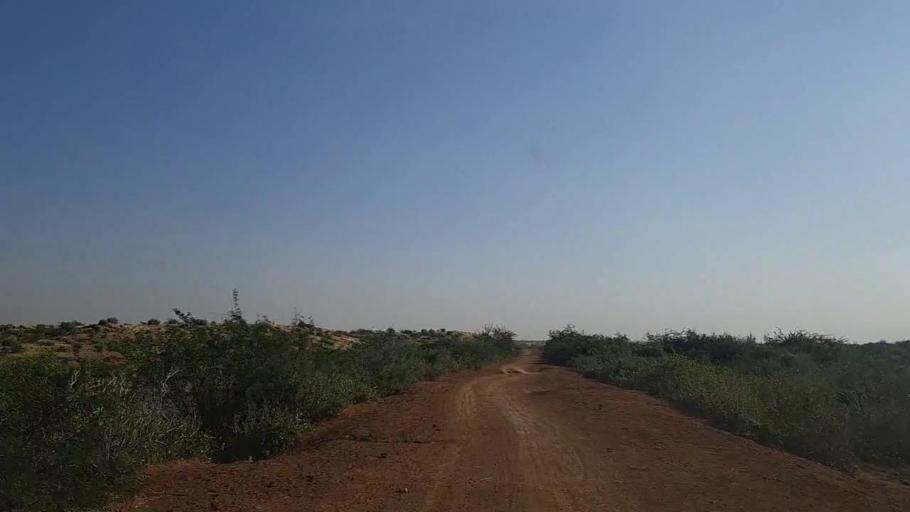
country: PK
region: Sindh
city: Daro Mehar
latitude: 25.0364
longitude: 68.1383
